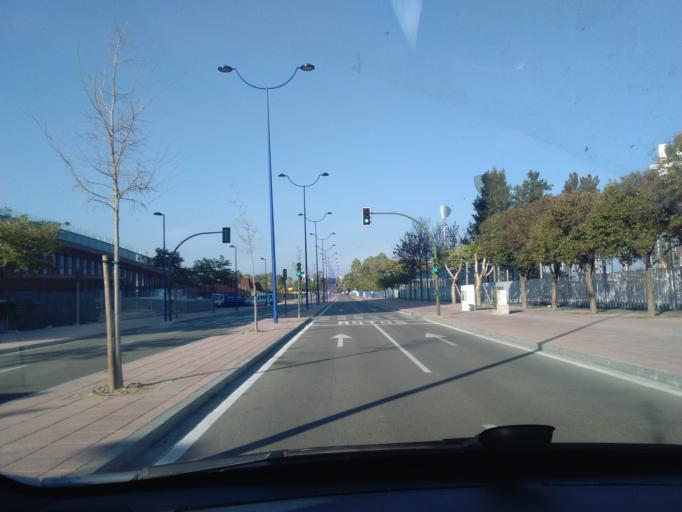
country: ES
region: Andalusia
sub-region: Provincia de Sevilla
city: Camas
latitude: 37.3916
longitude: -6.0092
